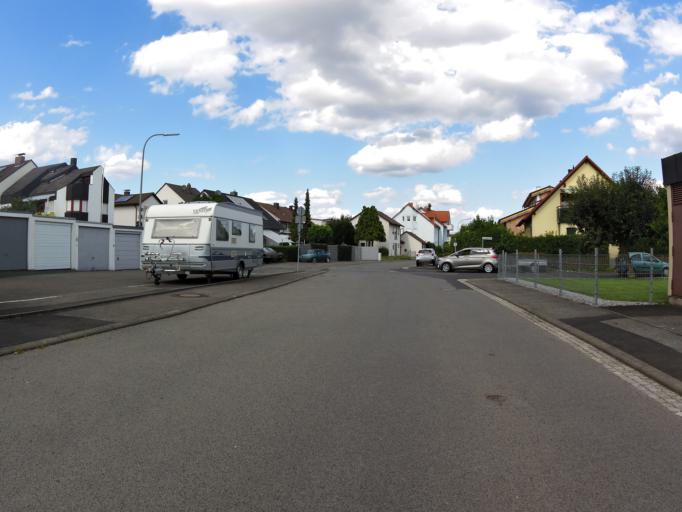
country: DE
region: Bavaria
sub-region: Regierungsbezirk Unterfranken
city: Bergrheinfeld
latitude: 50.0111
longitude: 10.1861
